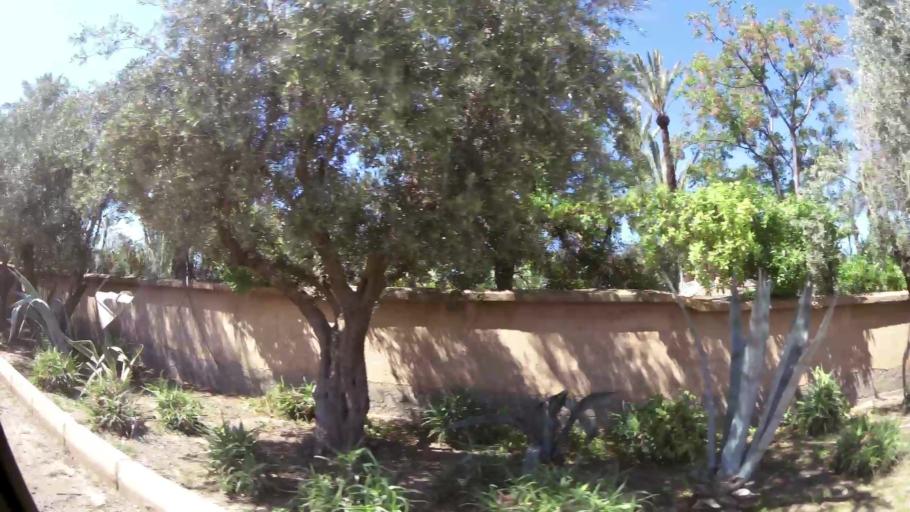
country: MA
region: Marrakech-Tensift-Al Haouz
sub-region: Marrakech
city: Marrakesh
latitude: 31.6746
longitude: -7.9856
